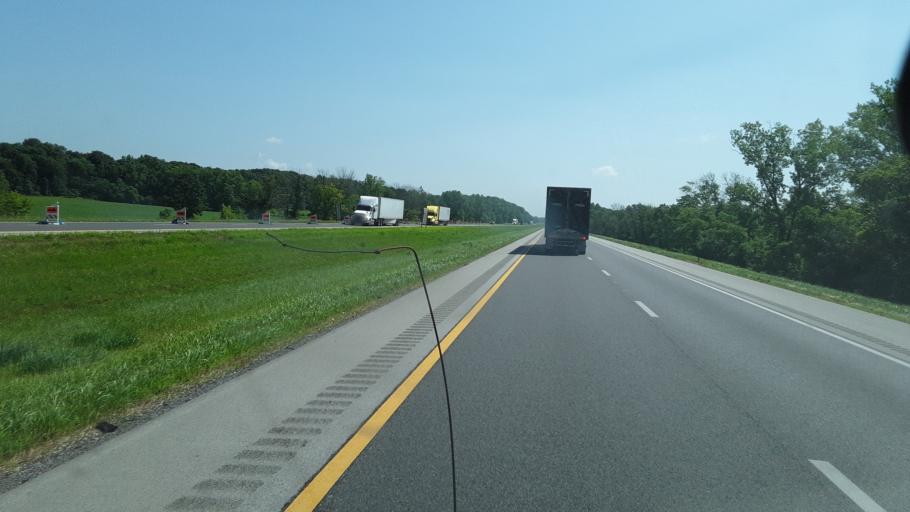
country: US
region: Illinois
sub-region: Cumberland County
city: Toledo
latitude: 39.2035
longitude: -88.2878
